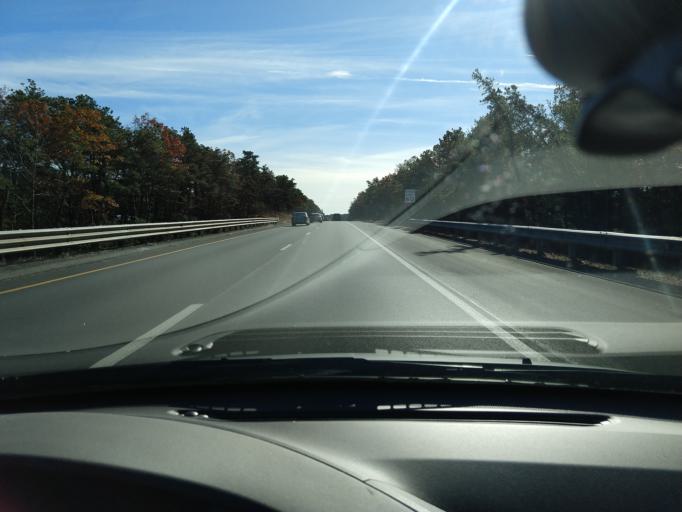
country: US
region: Massachusetts
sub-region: Plymouth County
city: Plymouth
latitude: 41.8948
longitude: -70.6142
